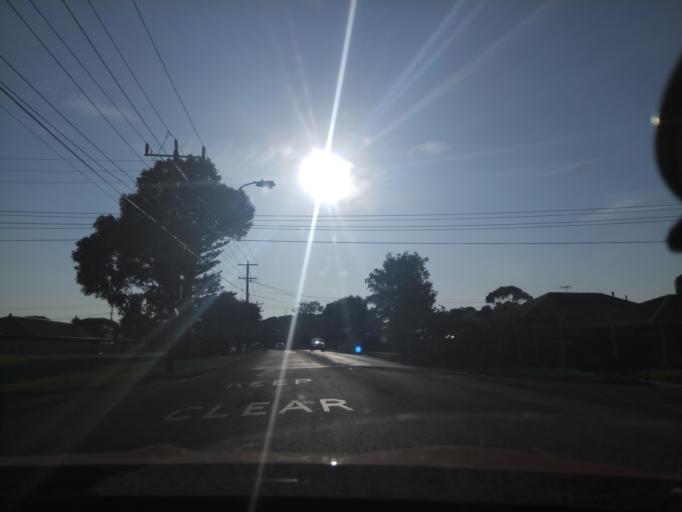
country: AU
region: Victoria
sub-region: Hobsons Bay
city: Laverton
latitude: -37.8703
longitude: 144.7628
